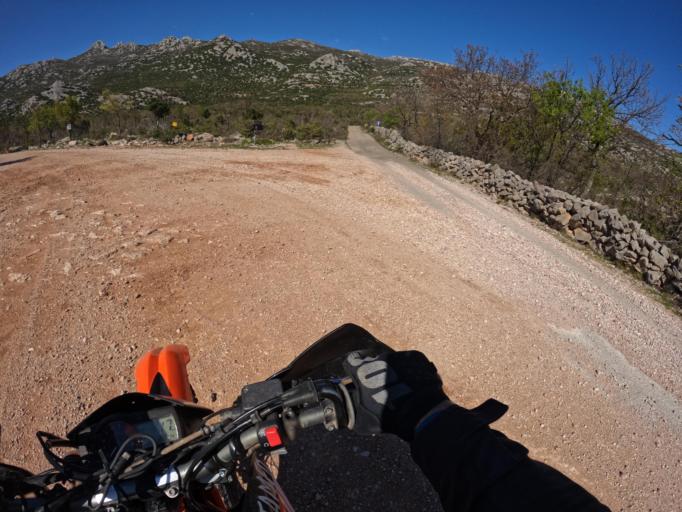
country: HR
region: Zadarska
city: Posedarje
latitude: 44.2633
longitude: 15.5511
